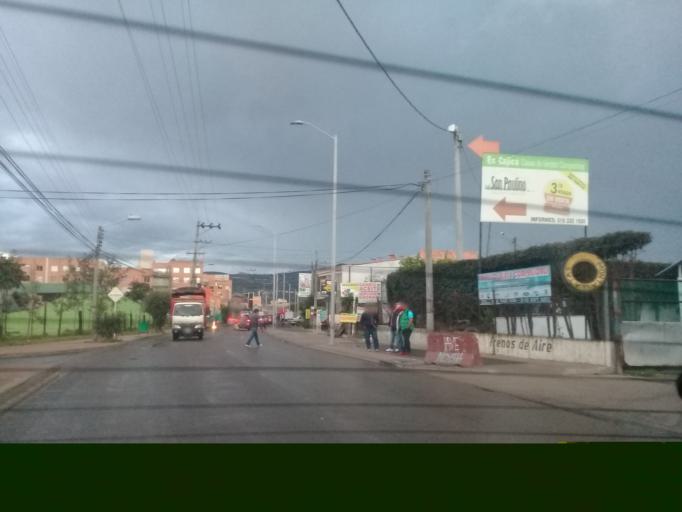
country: CO
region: Cundinamarca
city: Cajica
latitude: 4.9221
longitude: -74.0358
